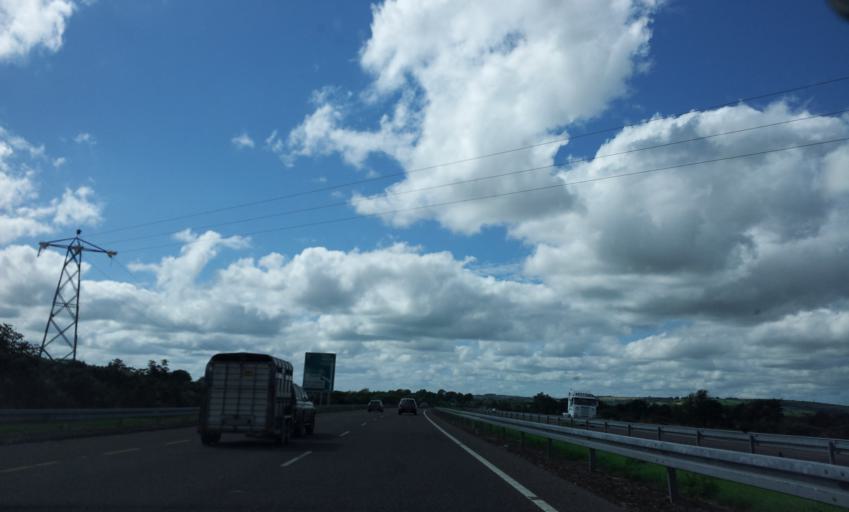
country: IE
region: Munster
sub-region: County Cork
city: Tower
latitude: 51.8726
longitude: -8.5928
